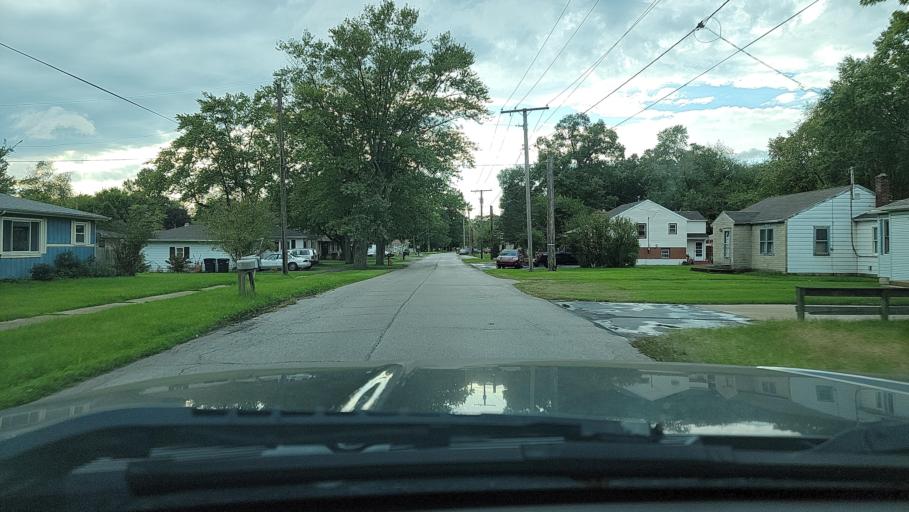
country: US
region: Indiana
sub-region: Porter County
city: Portage
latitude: 41.5719
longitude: -87.2036
